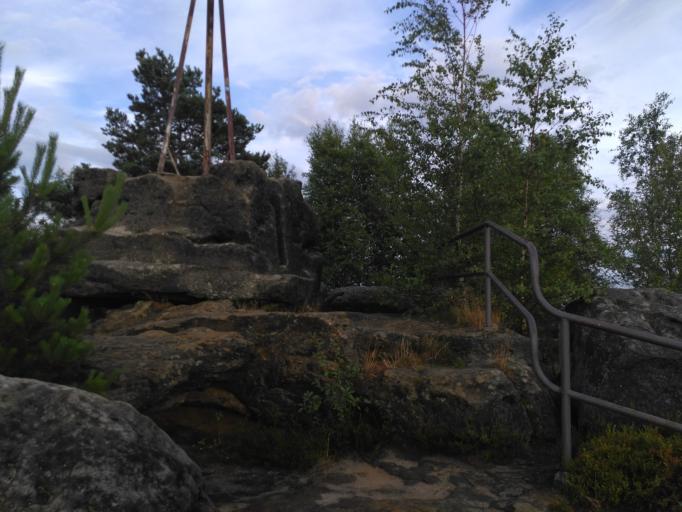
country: DE
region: Saxony
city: Bad Schandau
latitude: 50.8867
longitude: 14.2180
